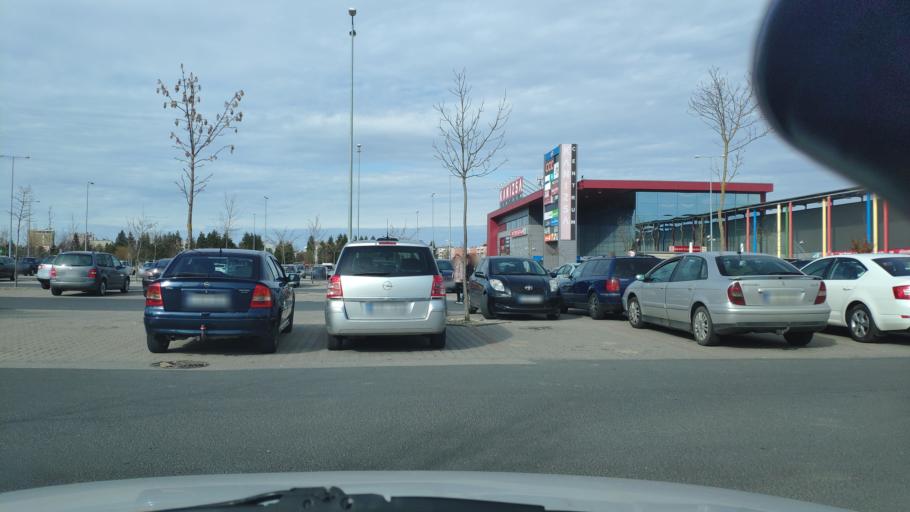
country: HU
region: Zala
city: Nagykanizsa
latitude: 46.4535
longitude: 17.0110
